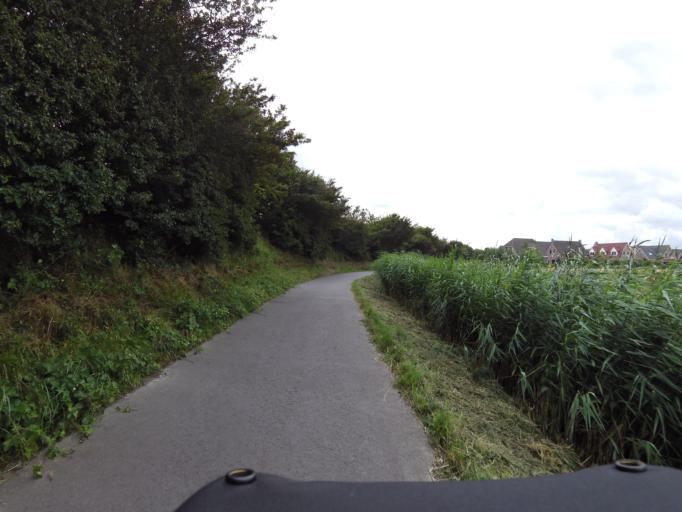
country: NL
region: South Holland
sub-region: Gemeente Goeree-Overflakkee
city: Goedereede
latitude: 51.8197
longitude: 3.9912
